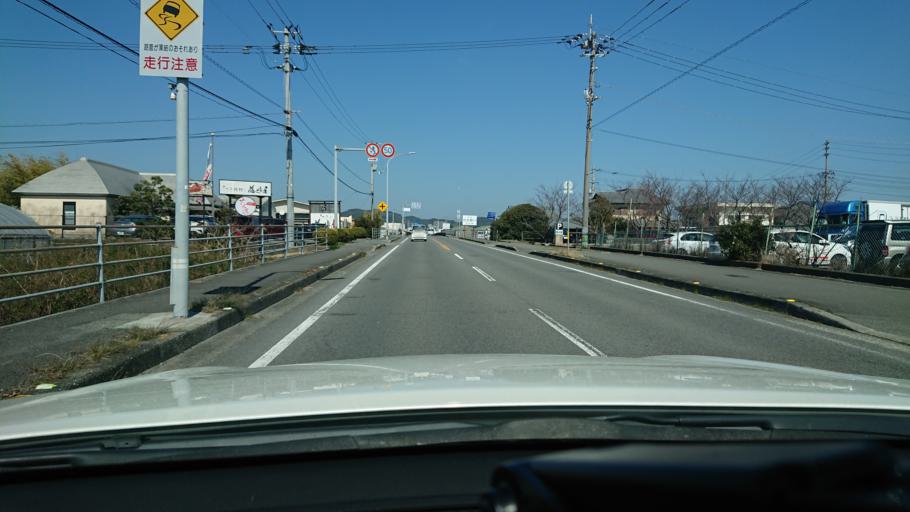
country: JP
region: Tokushima
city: Narutocho-mitsuishi
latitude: 34.1490
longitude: 134.5933
